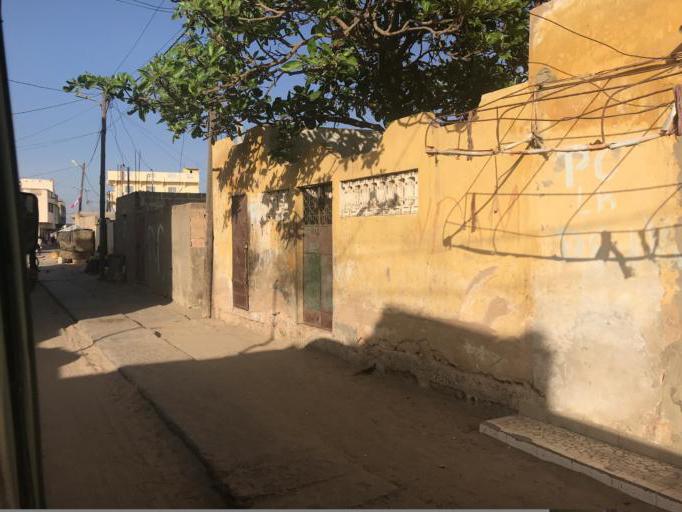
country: SN
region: Saint-Louis
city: Saint-Louis
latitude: 16.0061
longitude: -16.4949
